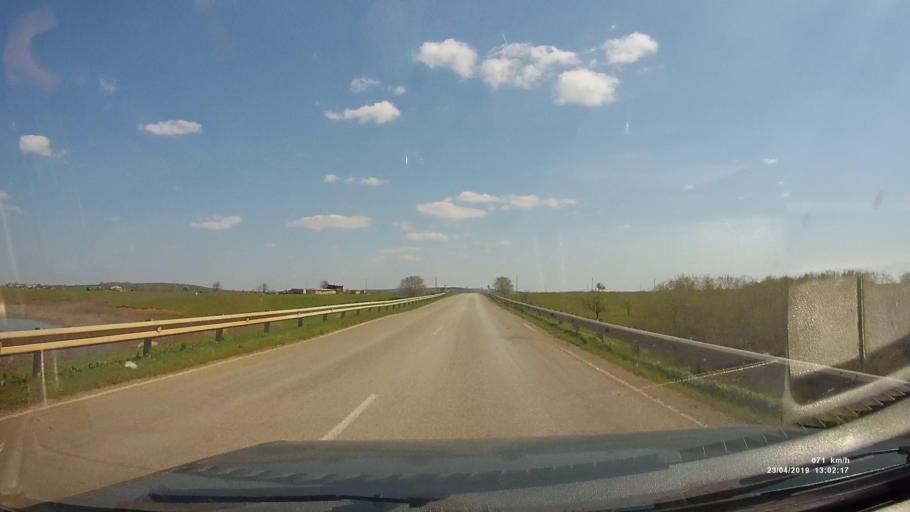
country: RU
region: Kalmykiya
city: Yashalta
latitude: 46.6011
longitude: 42.6672
